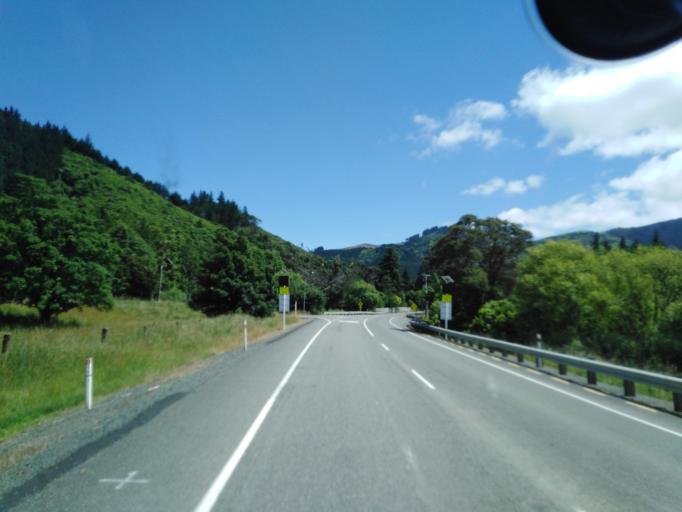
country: NZ
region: Nelson
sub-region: Nelson City
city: Nelson
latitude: -41.2182
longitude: 173.3966
